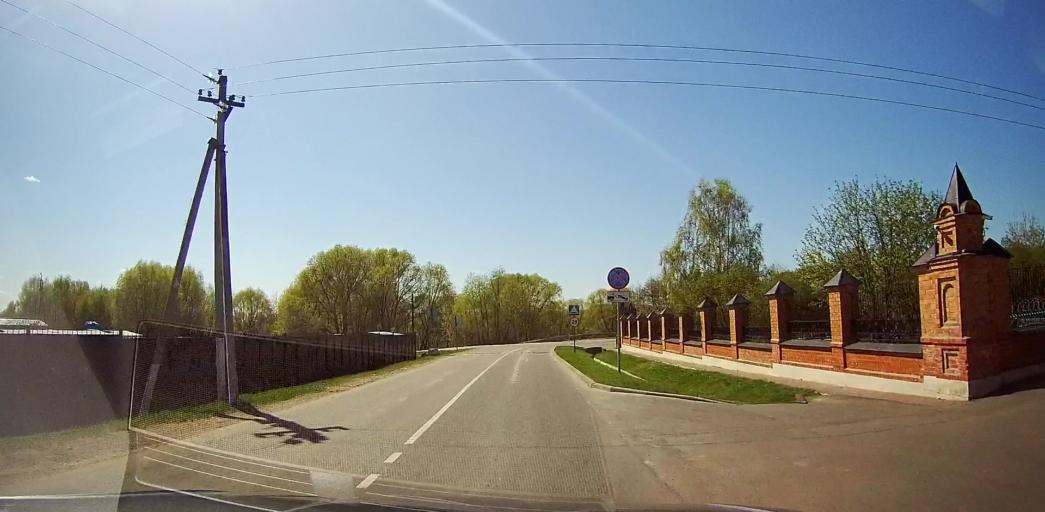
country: RU
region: Moskovskaya
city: Bronnitsy
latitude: 55.4562
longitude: 38.2340
